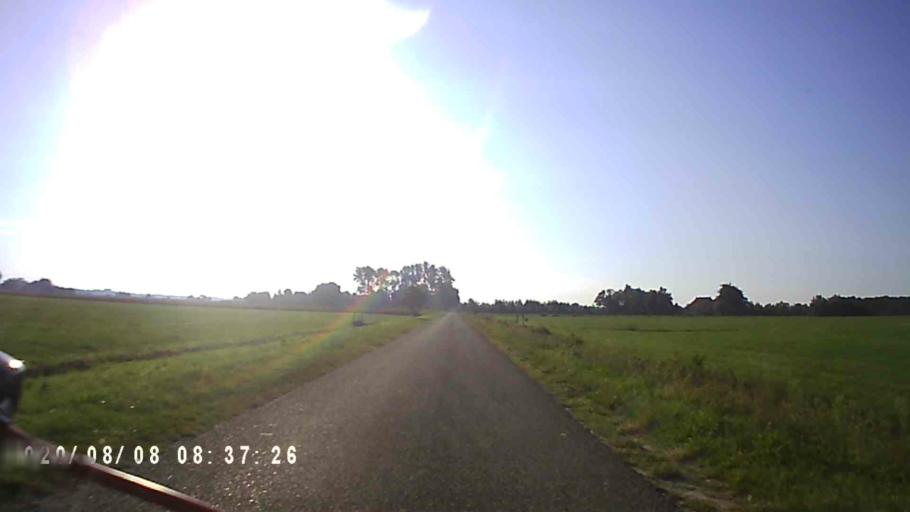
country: NL
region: Groningen
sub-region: Gemeente Leek
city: Leek
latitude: 53.0733
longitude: 6.3412
